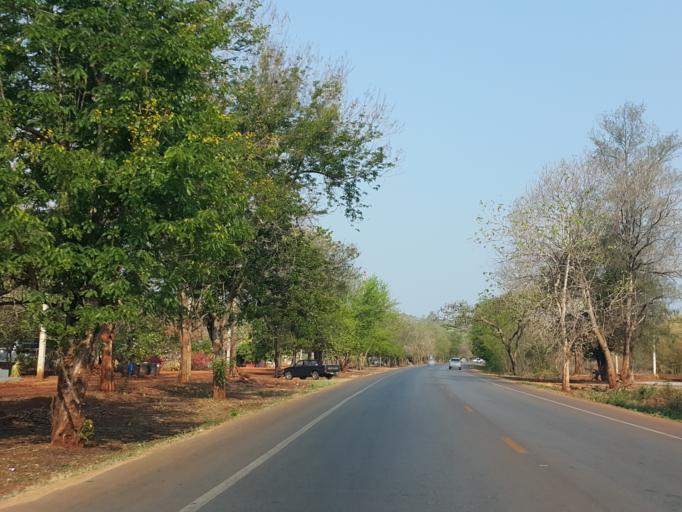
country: TH
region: Kanchanaburi
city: Sai Yok
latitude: 14.0991
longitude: 99.2344
